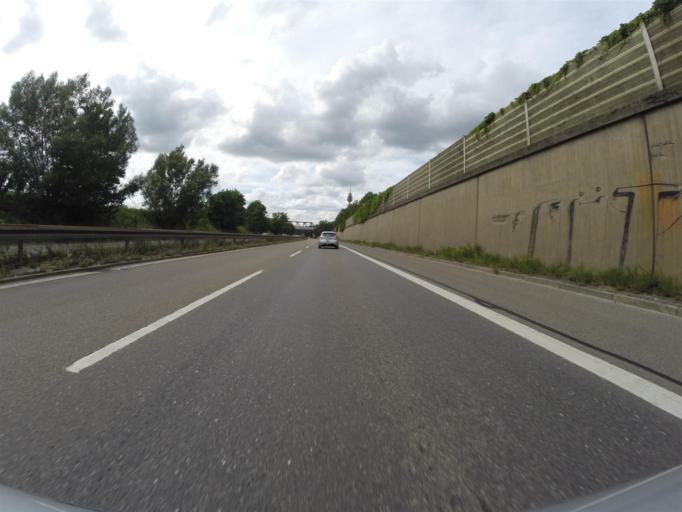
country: DE
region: Bavaria
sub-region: Regierungsbezirk Mittelfranken
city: Grossreuth bei Schweinau
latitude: 49.4168
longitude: 11.0565
